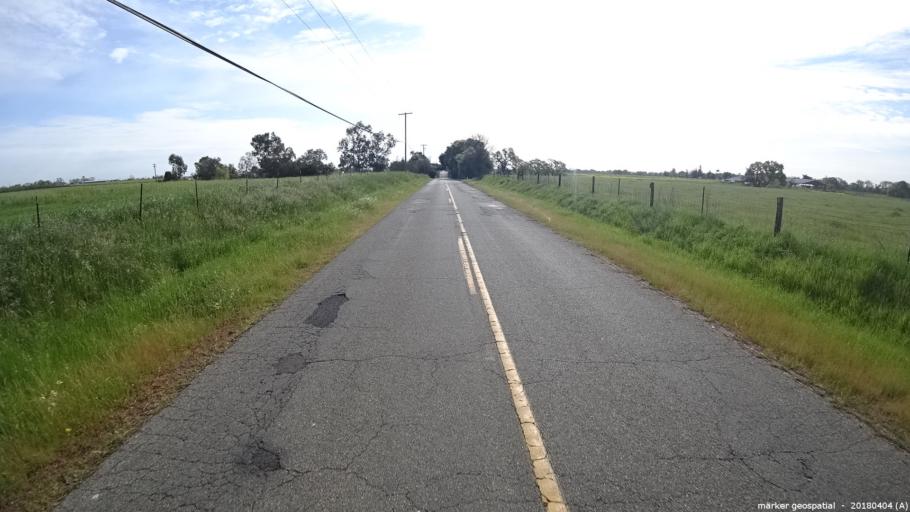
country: US
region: California
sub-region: Sacramento County
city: Galt
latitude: 38.2552
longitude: -121.2612
